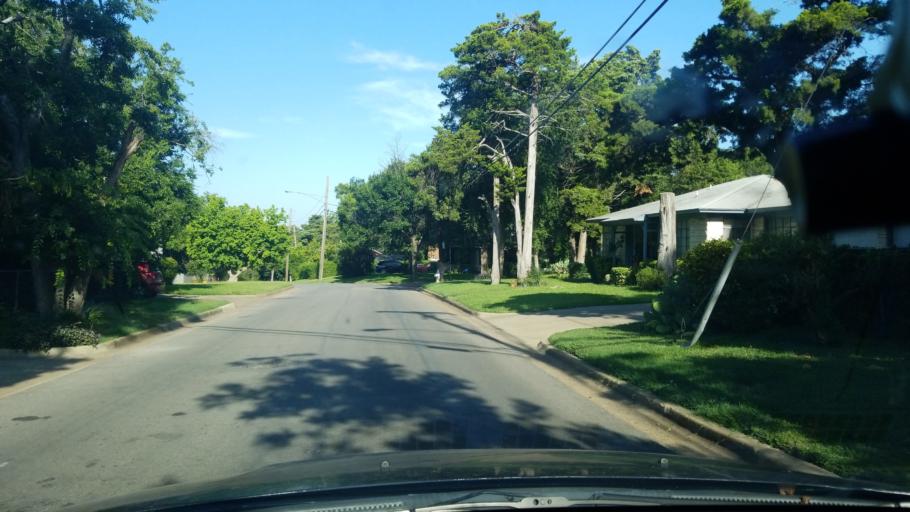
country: US
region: Texas
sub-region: Dallas County
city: Dallas
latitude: 32.7295
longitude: -96.8173
